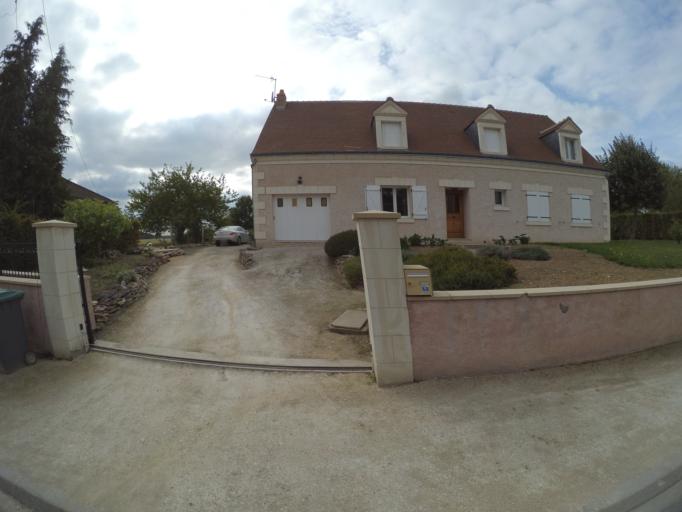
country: FR
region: Centre
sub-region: Departement d'Indre-et-Loire
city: Nazelles-Negron
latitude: 47.4859
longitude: 0.9467
